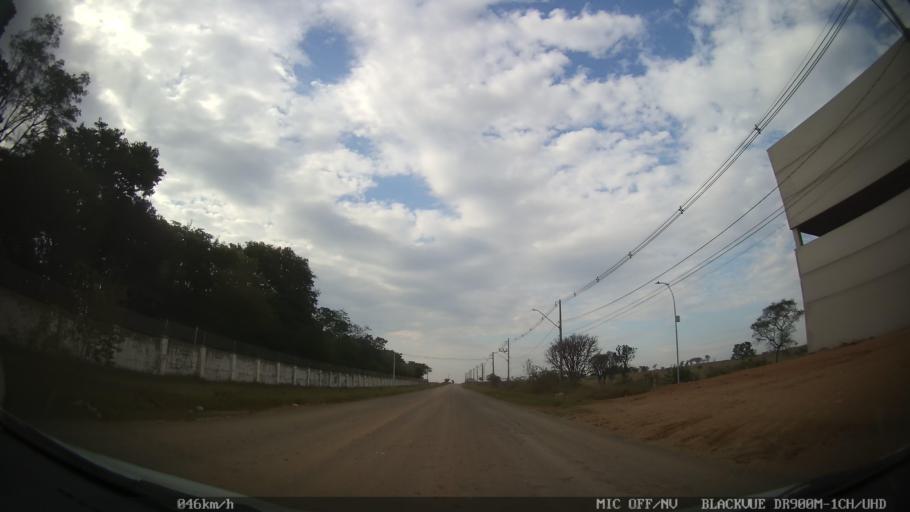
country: BR
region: Sao Paulo
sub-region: Paulinia
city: Paulinia
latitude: -22.7215
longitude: -47.1610
